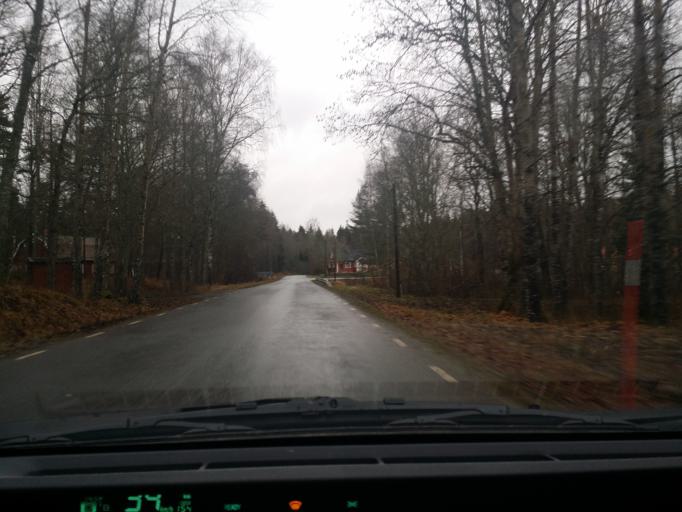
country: SE
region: Vaestmanland
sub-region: Vasteras
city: Skultuna
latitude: 59.7802
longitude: 16.3774
